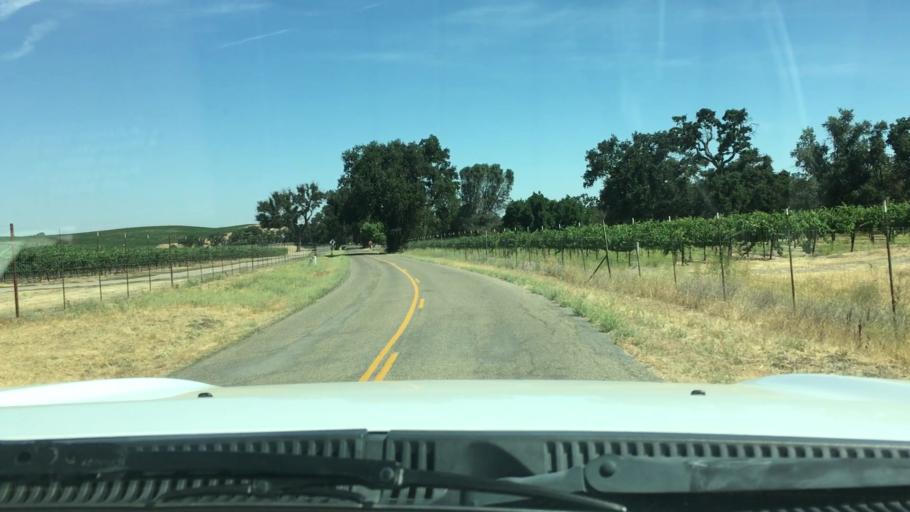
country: US
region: California
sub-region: San Luis Obispo County
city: Templeton
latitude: 35.5694
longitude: -120.6072
